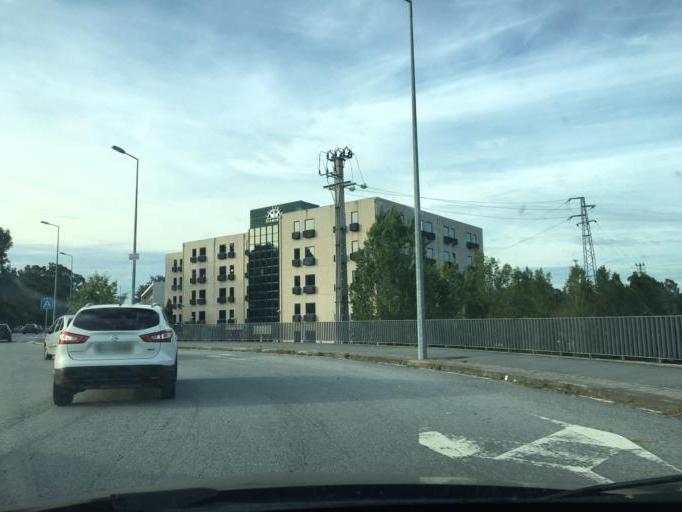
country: PT
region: Porto
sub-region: Maia
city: Maia
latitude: 41.2346
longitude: -8.6399
